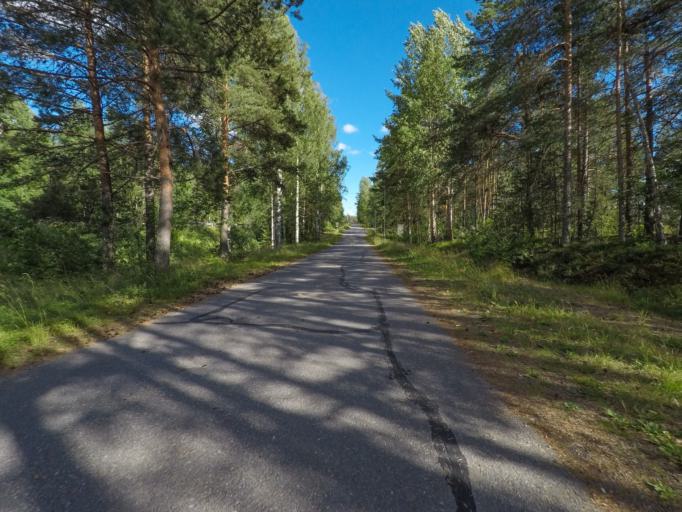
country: FI
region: South Karelia
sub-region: Lappeenranta
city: Lappeenranta
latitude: 61.0991
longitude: 28.1317
